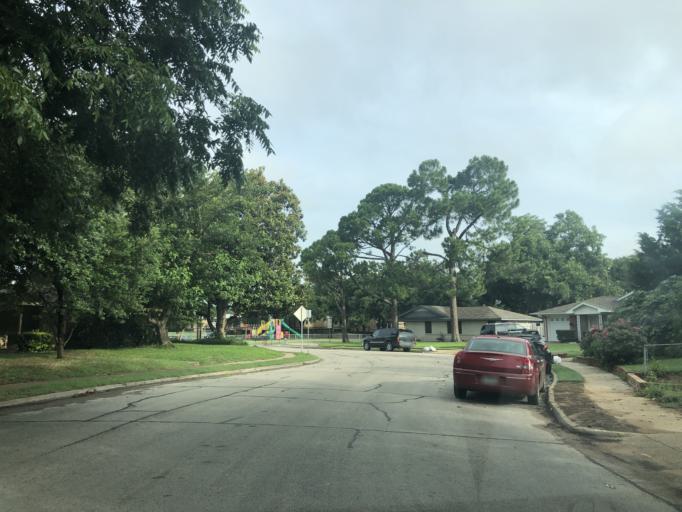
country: US
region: Texas
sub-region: Dallas County
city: Irving
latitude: 32.8043
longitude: -96.9787
